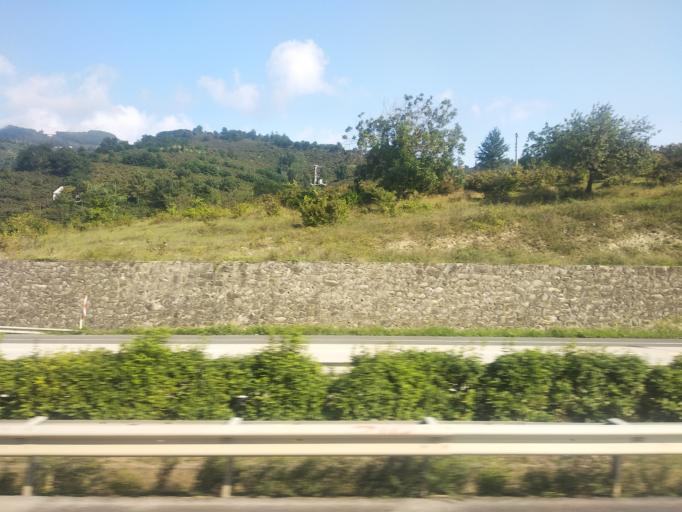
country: TR
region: Ordu
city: Ordu
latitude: 41.0043
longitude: 37.8264
